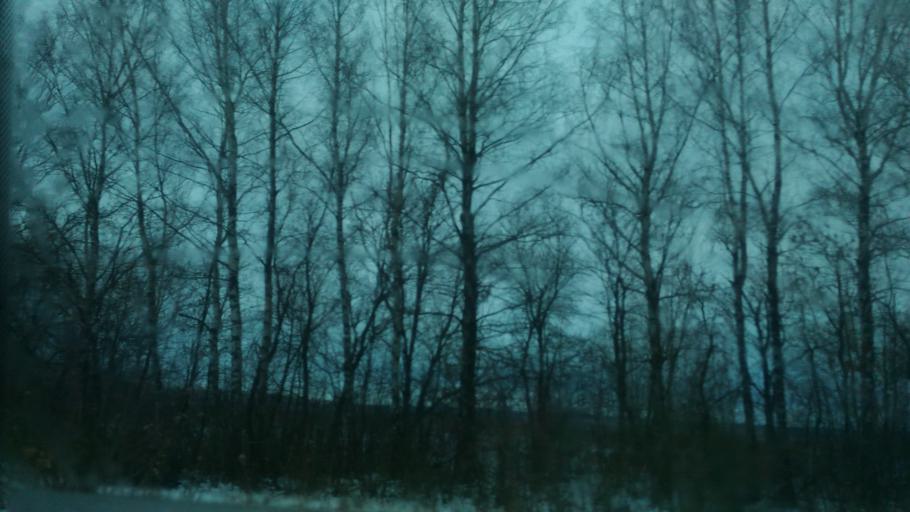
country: RU
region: Tula
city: Bolokhovo
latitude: 54.0858
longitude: 37.7762
